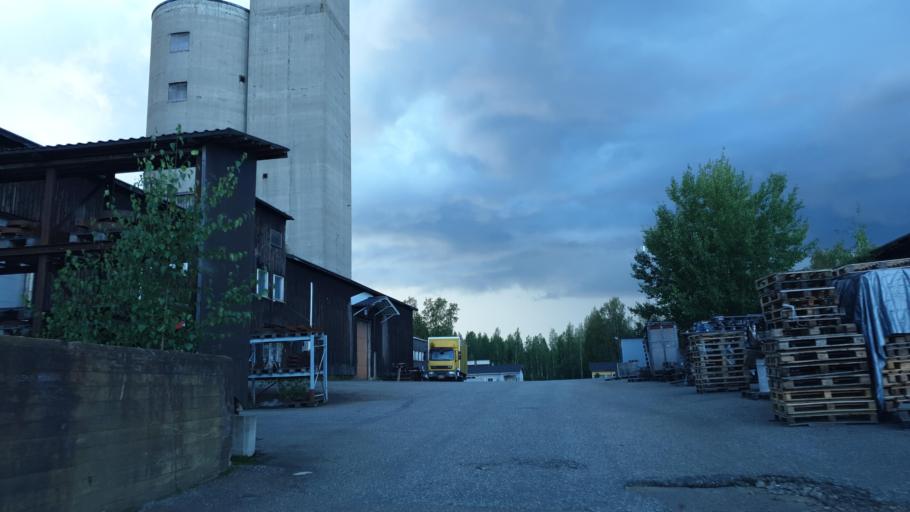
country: FI
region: Northern Savo
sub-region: Varkaus
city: Leppaevirta
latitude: 62.5799
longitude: 27.6094
